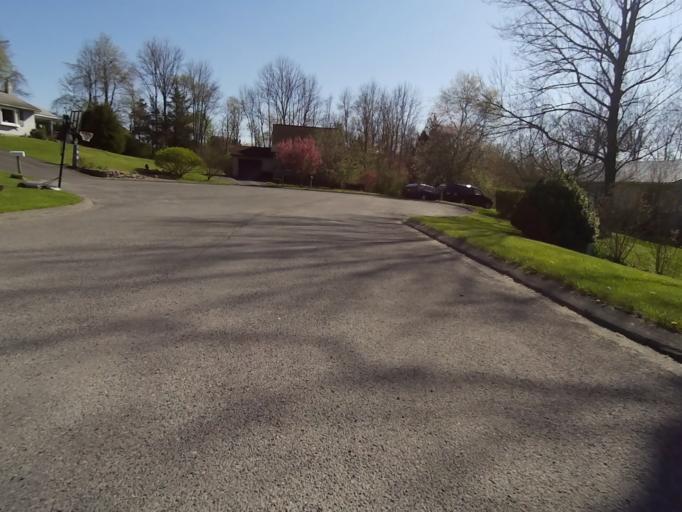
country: US
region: Pennsylvania
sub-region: Centre County
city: Bellefonte
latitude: 40.9100
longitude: -77.7898
